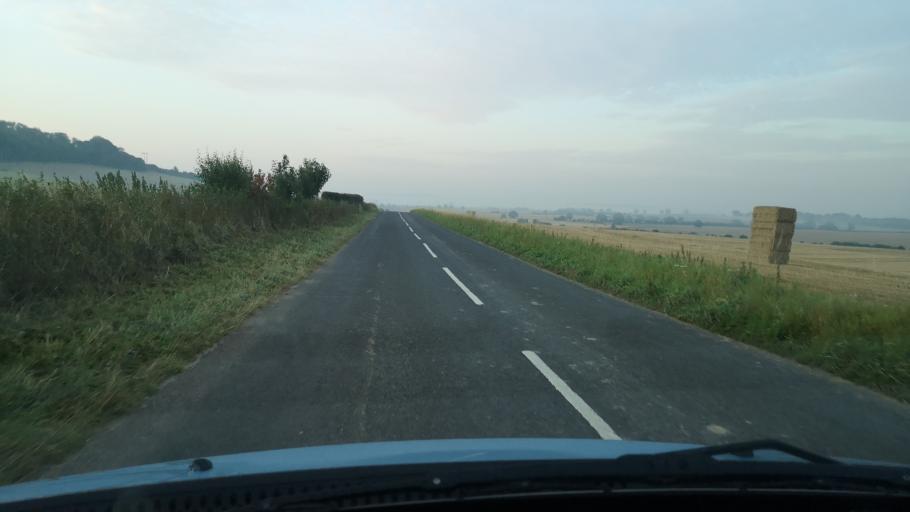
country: GB
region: England
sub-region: City and Borough of Wakefield
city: Darrington
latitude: 53.6686
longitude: -1.2876
